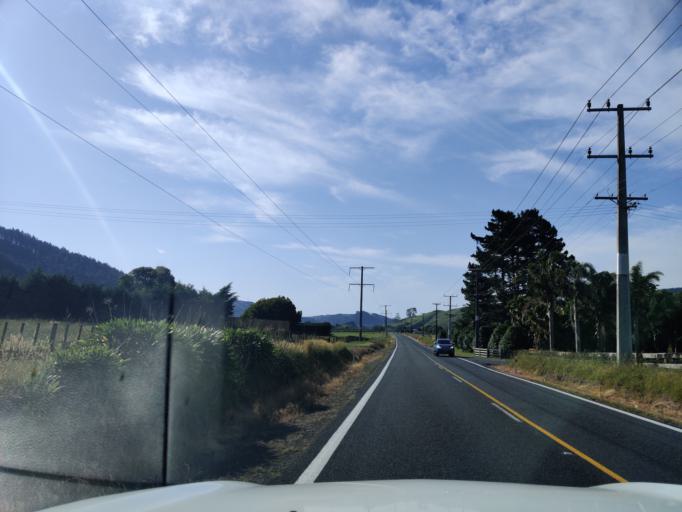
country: NZ
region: Waikato
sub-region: Waikato District
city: Ngaruawahia
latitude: -37.6117
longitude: 175.1792
